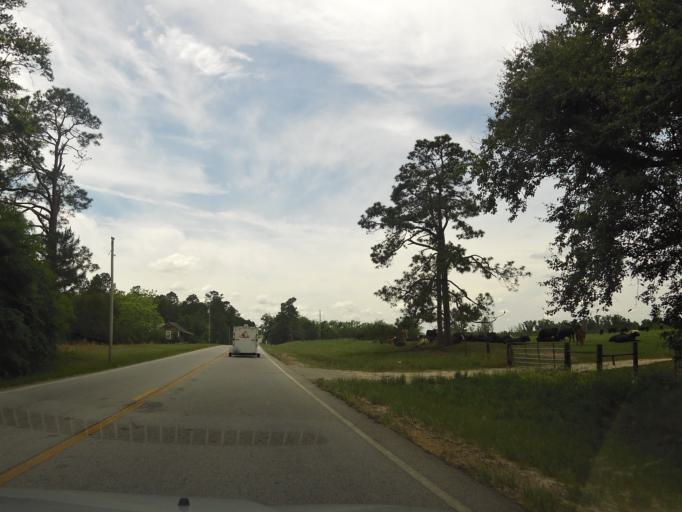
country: US
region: Georgia
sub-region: Emanuel County
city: Swainsboro
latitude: 32.5213
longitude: -82.2908
